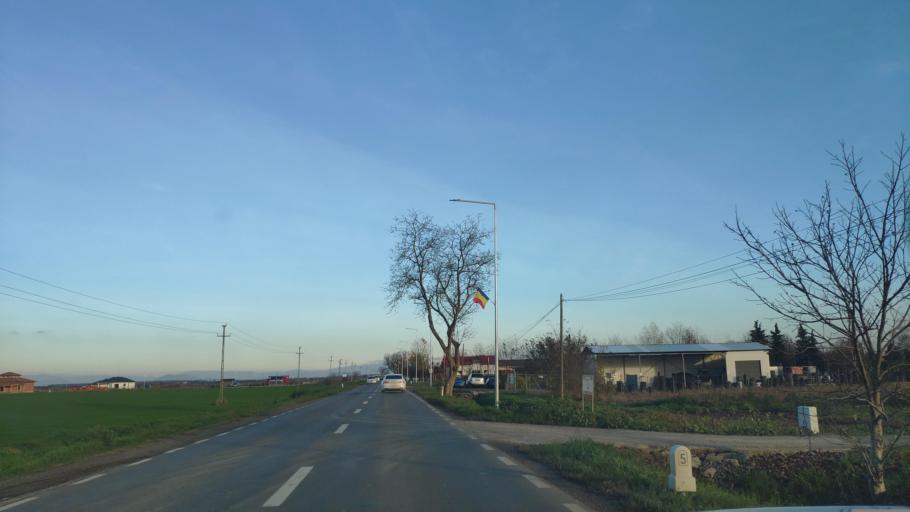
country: RO
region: Satu Mare
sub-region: Comuna Paulesti
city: Paulesti
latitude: 47.7975
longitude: 22.9459
